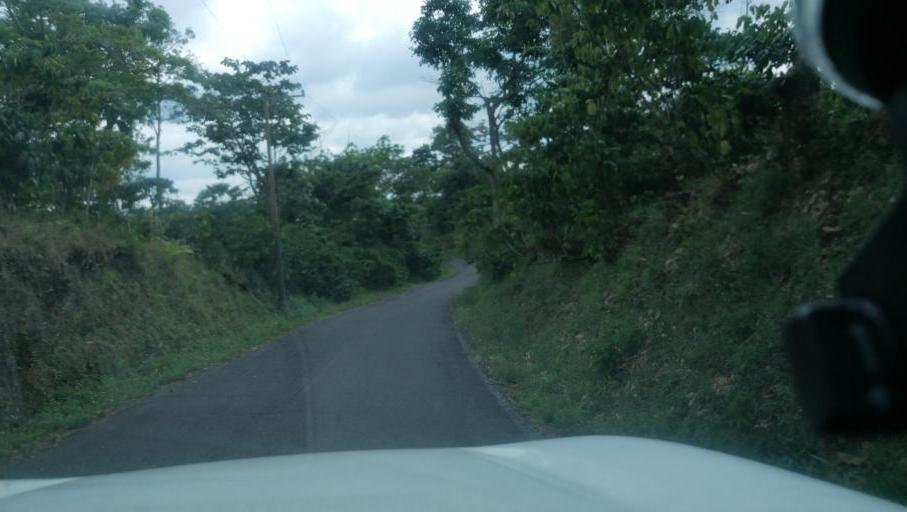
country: MX
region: Chiapas
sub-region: Cacahoatan
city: Benito Juarez
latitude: 15.0582
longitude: -92.1512
